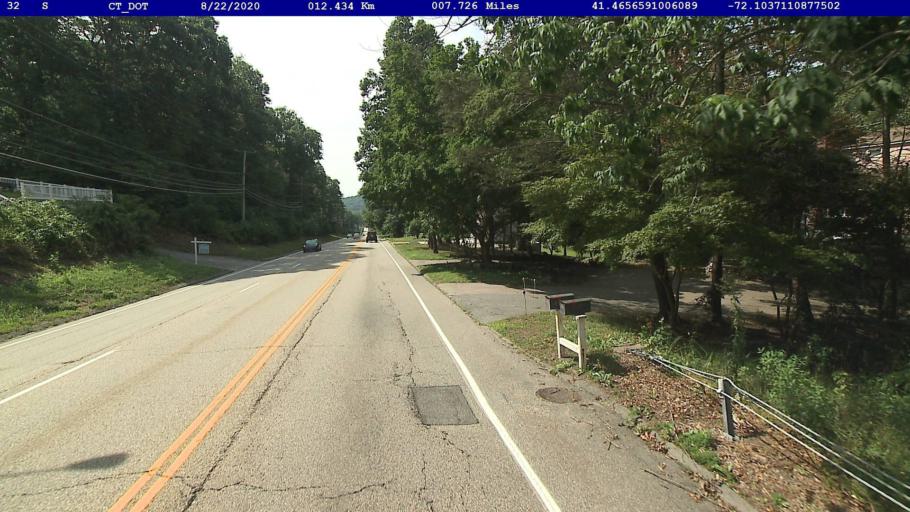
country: US
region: Connecticut
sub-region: New London County
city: Oxoboxo River
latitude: 41.4657
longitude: -72.1037
